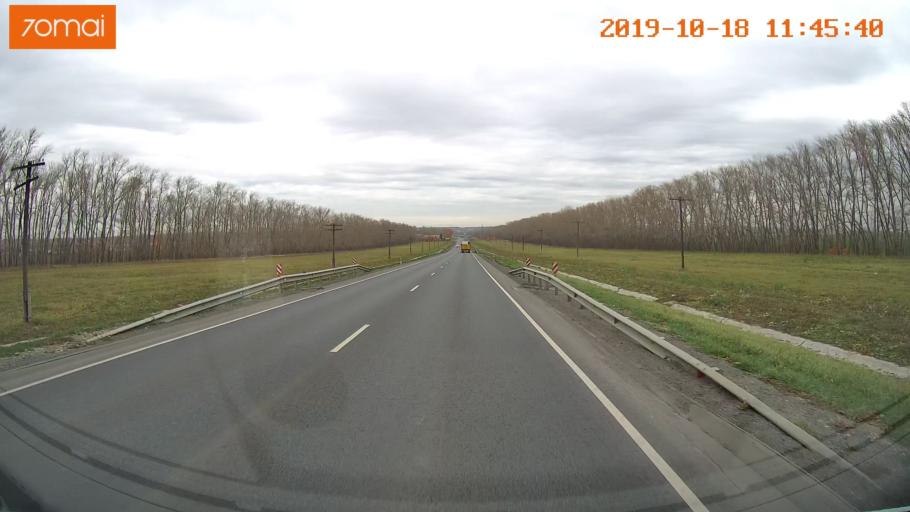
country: RU
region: Rjazan
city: Mikhaylov
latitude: 54.2125
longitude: 38.9730
